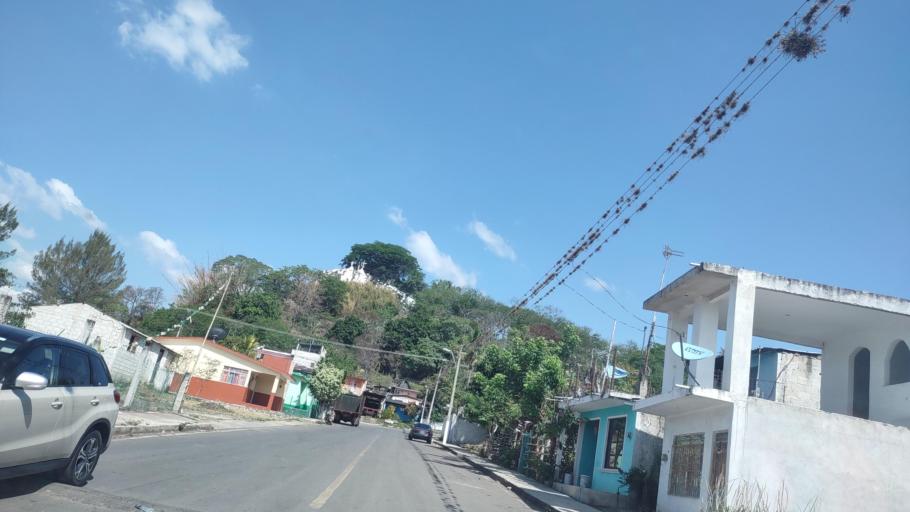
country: MX
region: Veracruz
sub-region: Coatepec
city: Tuzamapan
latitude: 19.3825
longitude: -96.9035
